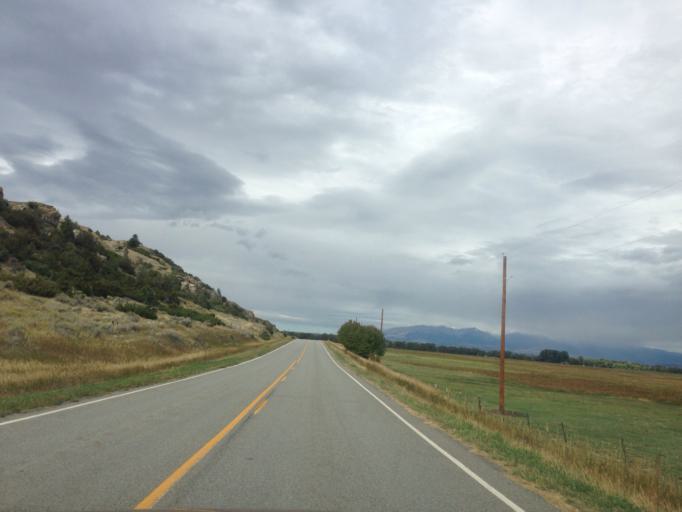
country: US
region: Montana
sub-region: Sweet Grass County
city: Big Timber
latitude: 45.7803
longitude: -109.8187
